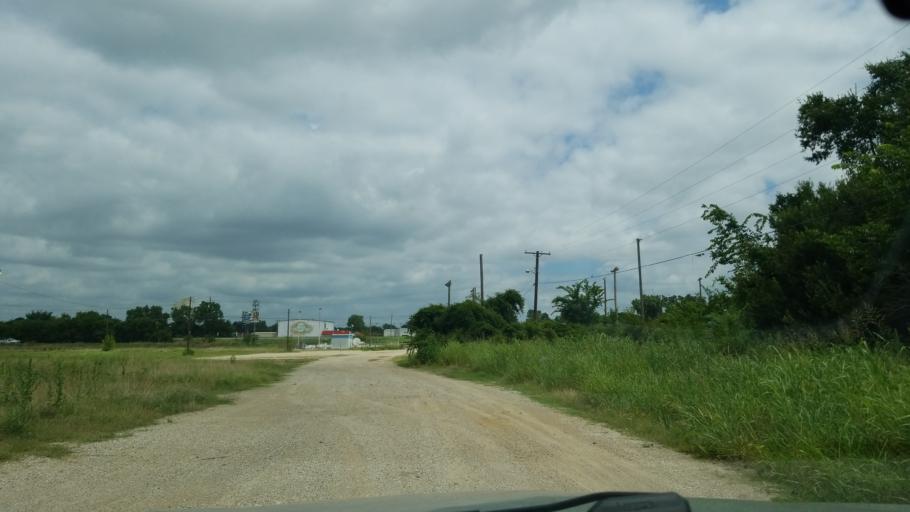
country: US
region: Texas
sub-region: Dallas County
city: Farmers Branch
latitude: 32.9497
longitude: -96.9401
